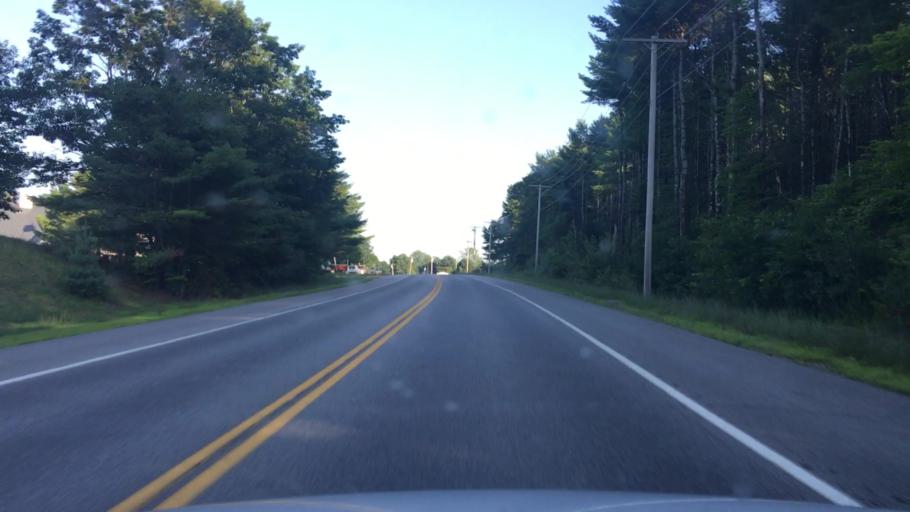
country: US
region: Maine
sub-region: Androscoggin County
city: Lisbon
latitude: 44.0261
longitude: -70.1012
